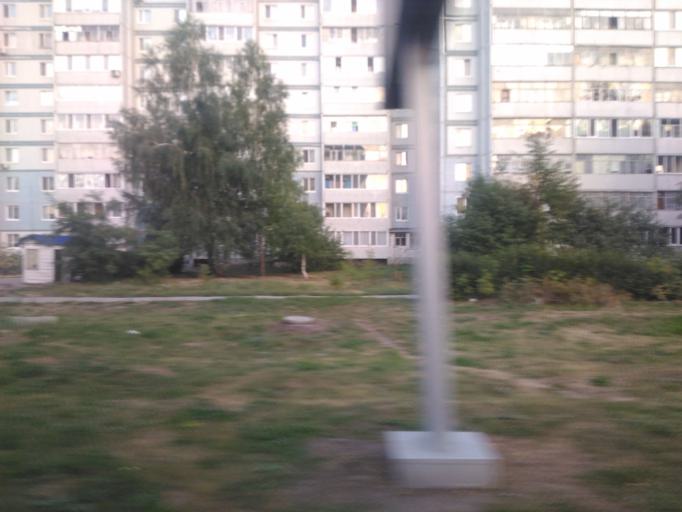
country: RU
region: Ulyanovsk
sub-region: Ulyanovskiy Rayon
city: Ulyanovsk
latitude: 54.2689
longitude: 48.2851
